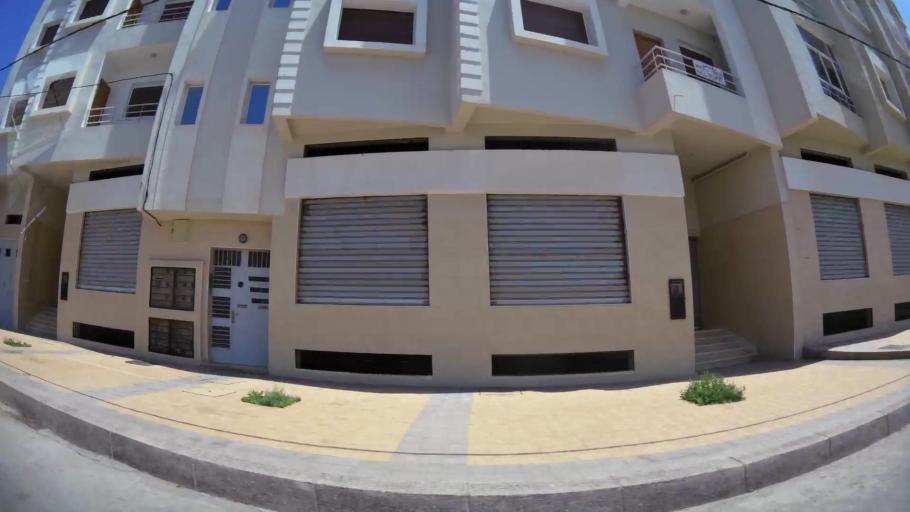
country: MA
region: Oriental
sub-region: Oujda-Angad
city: Oujda
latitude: 34.6852
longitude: -1.8936
